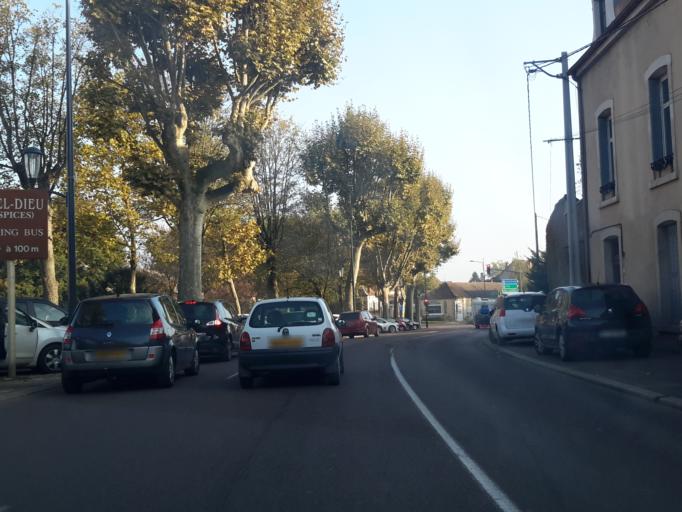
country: FR
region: Bourgogne
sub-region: Departement de la Cote-d'Or
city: Beaune
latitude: 47.0214
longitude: 4.8345
